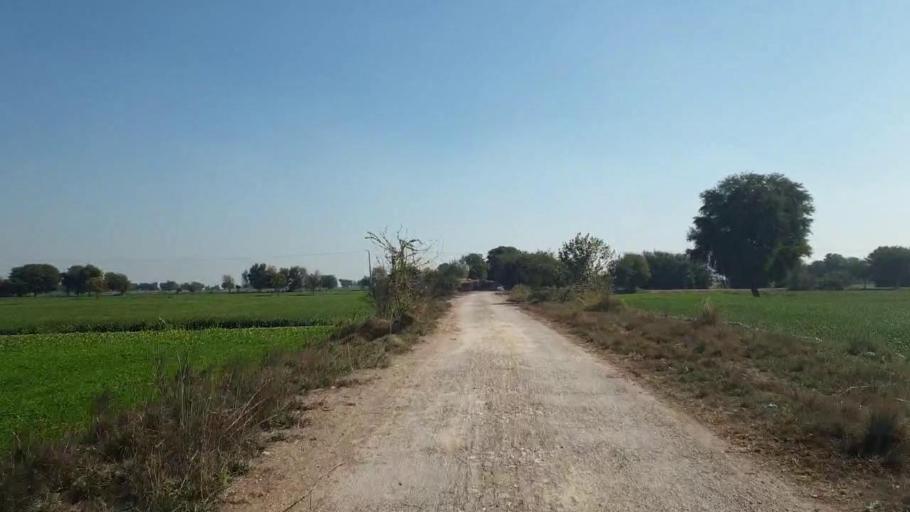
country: PK
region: Sindh
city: Shahpur Chakar
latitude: 26.1281
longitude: 68.6396
